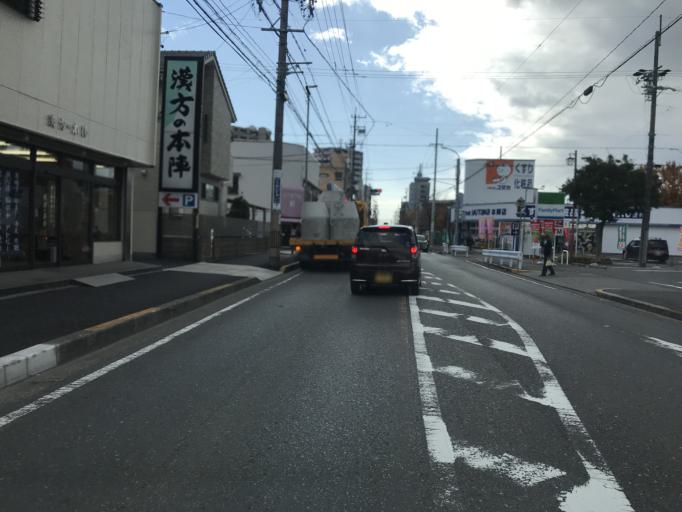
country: JP
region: Aichi
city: Nagoya-shi
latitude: 35.1772
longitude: 136.8637
